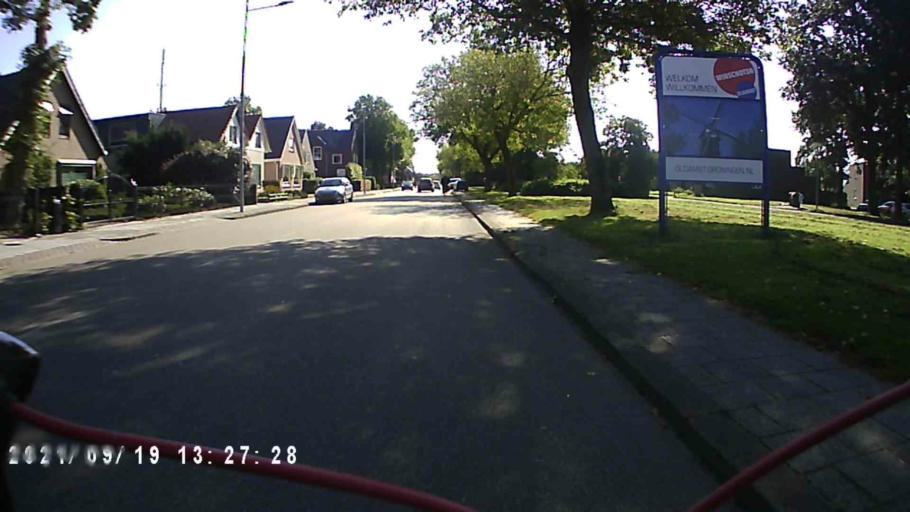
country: NL
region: Groningen
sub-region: Gemeente  Oldambt
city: Winschoten
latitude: 53.1510
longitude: 7.0205
